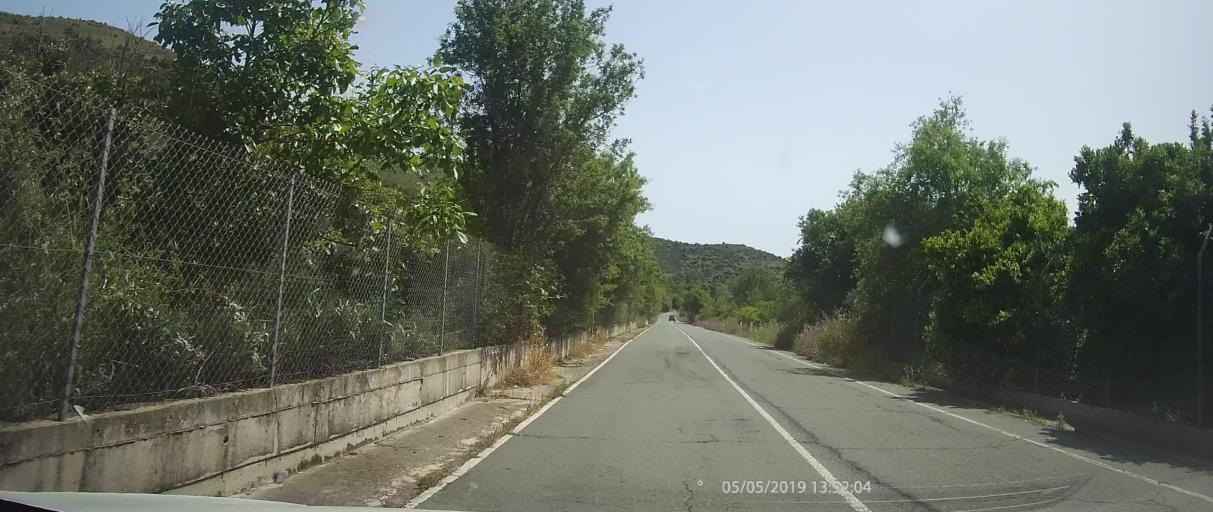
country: CY
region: Limassol
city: Pachna
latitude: 34.8329
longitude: 32.7360
